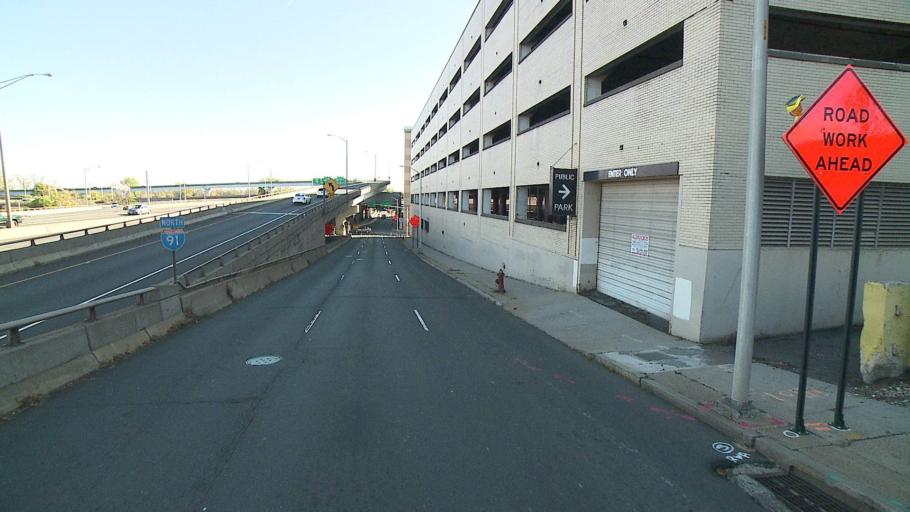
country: US
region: Connecticut
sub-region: Hartford County
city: Hartford
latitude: 41.7694
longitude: -72.6722
